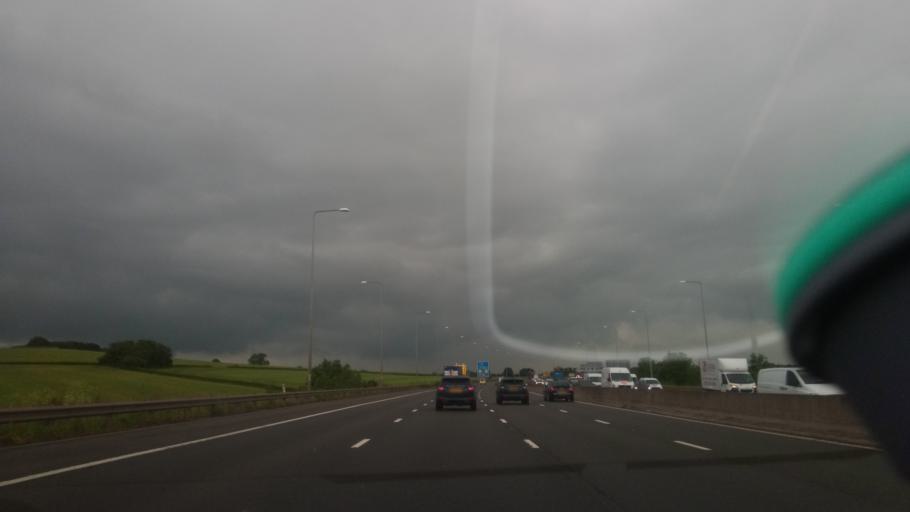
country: GB
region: England
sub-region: Nottinghamshire
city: Kimberley
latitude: 52.9723
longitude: -1.2540
